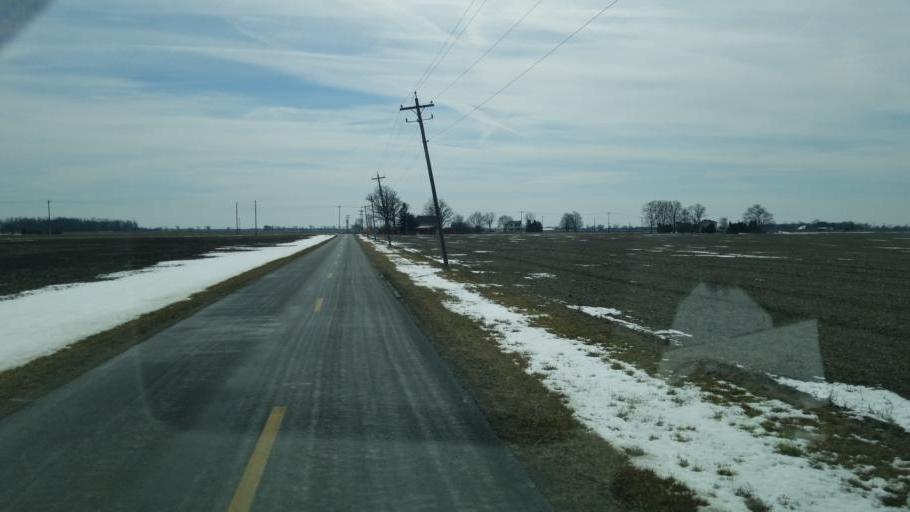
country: US
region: Ohio
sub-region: Delaware County
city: Delaware
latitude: 40.3356
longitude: -82.9980
